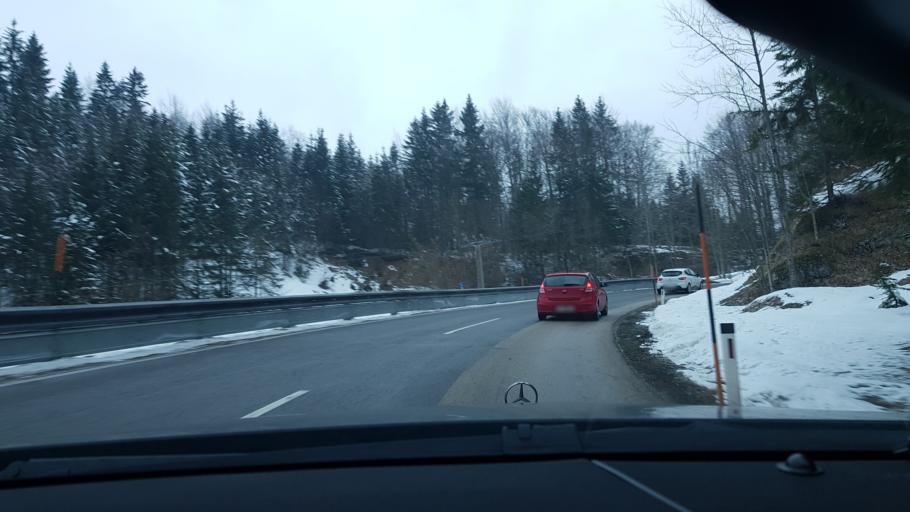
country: AT
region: Lower Austria
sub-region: Politischer Bezirk Scheibbs
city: Lunz am See
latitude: 47.8792
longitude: 15.0672
